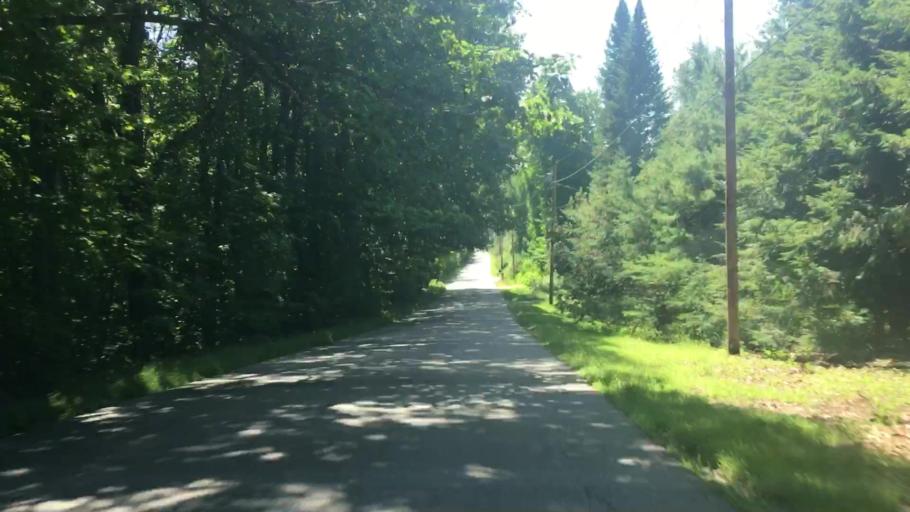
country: US
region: Maine
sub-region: Kennebec County
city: Monmouth
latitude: 44.1963
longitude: -69.9646
